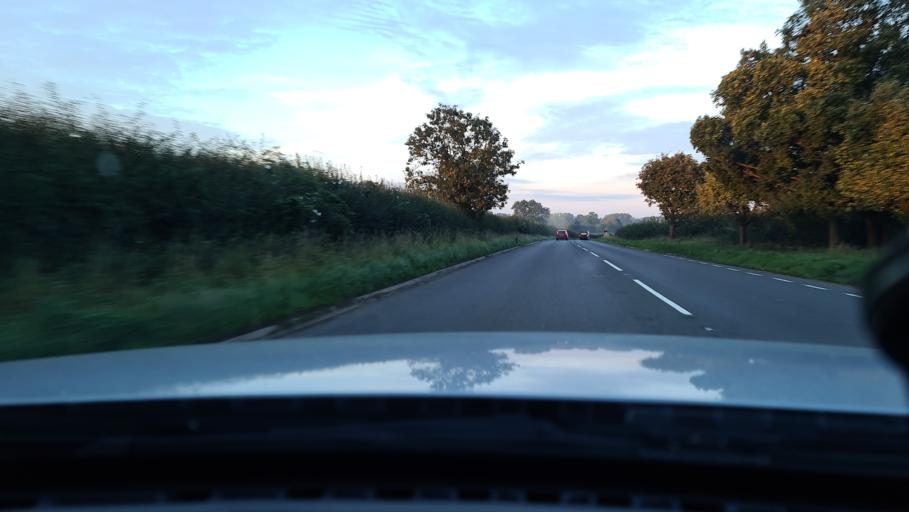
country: GB
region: England
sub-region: Leicestershire
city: Sapcote
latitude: 52.5286
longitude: -1.2735
